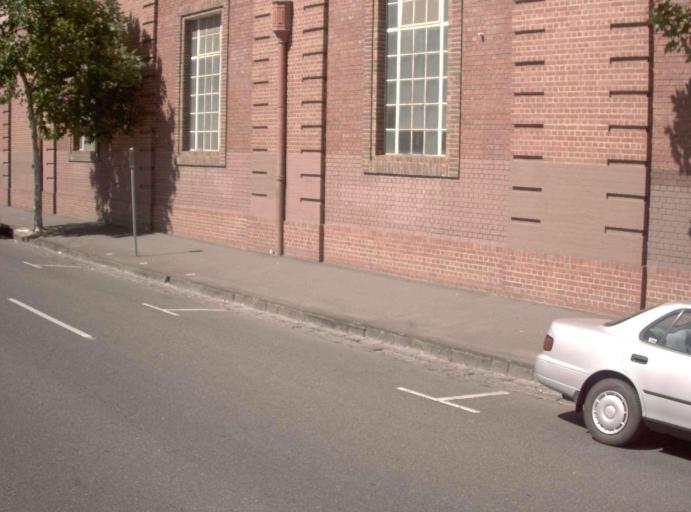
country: AU
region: Victoria
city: Glenferrie
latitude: -37.8294
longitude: 145.0545
